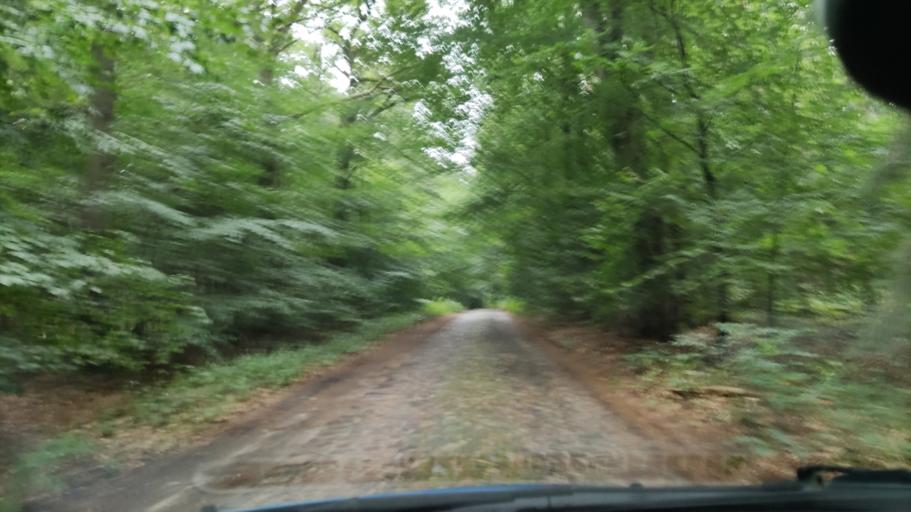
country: DE
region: Lower Saxony
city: Altenmedingen
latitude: 53.1506
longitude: 10.5820
